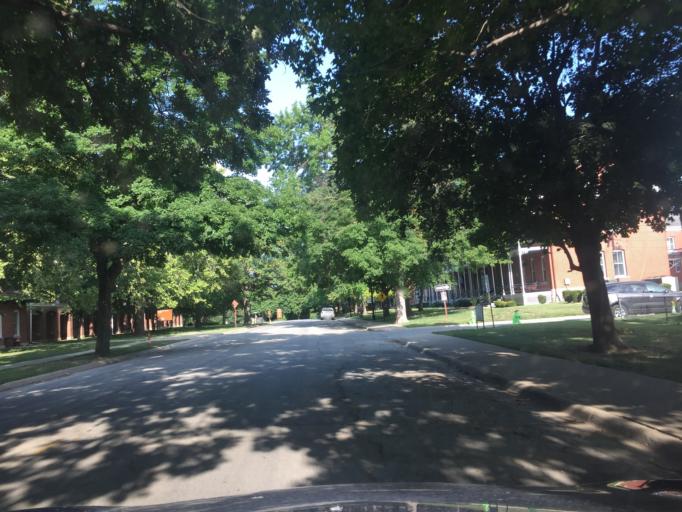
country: US
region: Kansas
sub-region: Leavenworth County
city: Leavenworth
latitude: 39.3556
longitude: -94.9217
